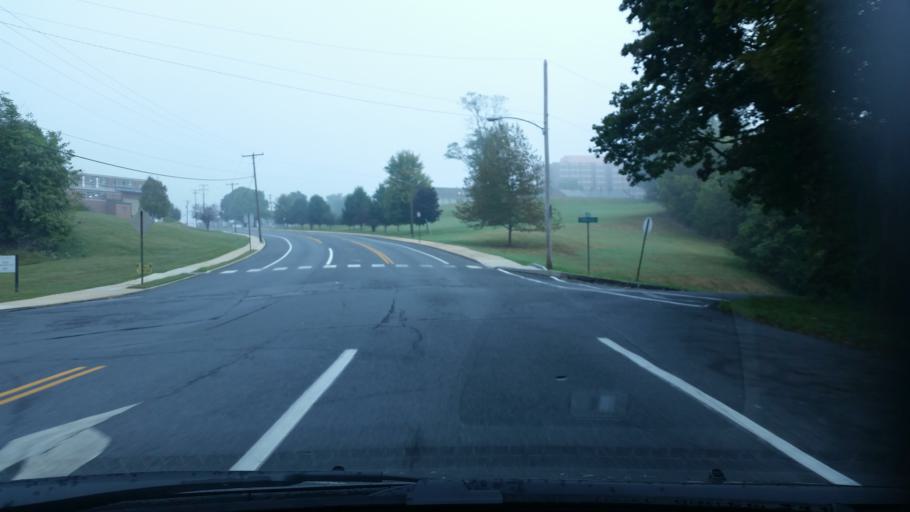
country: US
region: Pennsylvania
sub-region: Lancaster County
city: Lancaster
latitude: 40.0357
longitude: -76.2869
